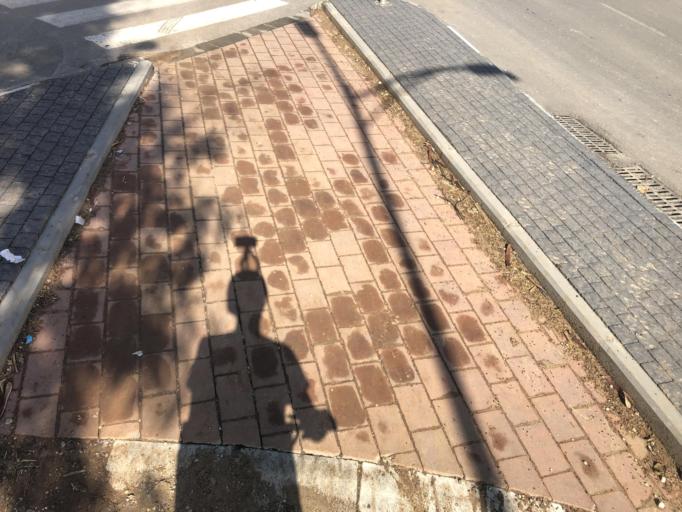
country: IL
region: Jerusalem
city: Modiin Ilit
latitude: 31.9272
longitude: 35.0460
